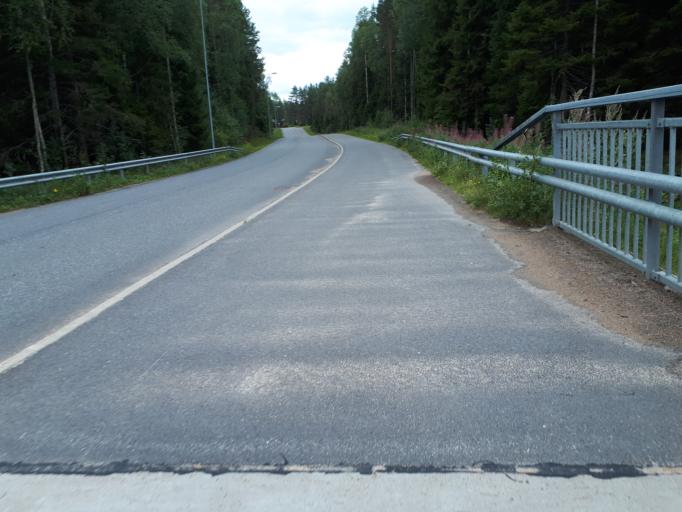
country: FI
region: Northern Ostrobothnia
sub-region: Oulunkaari
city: Ii
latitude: 65.3219
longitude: 25.4100
